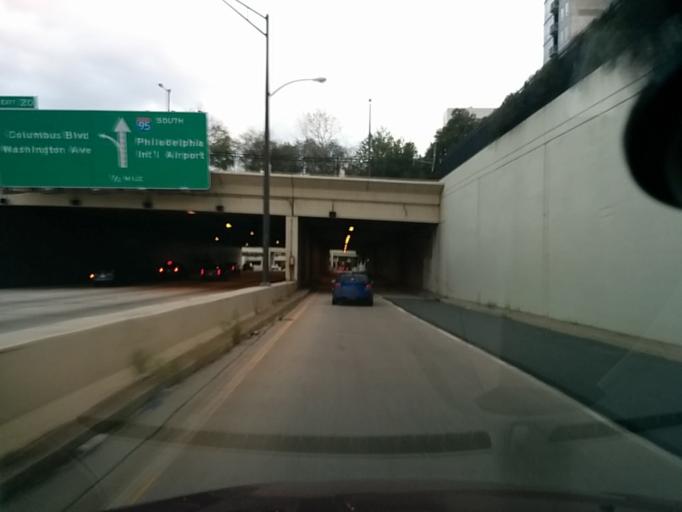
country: US
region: Pennsylvania
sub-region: Philadelphia County
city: Philadelphia
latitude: 39.9485
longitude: -75.1422
